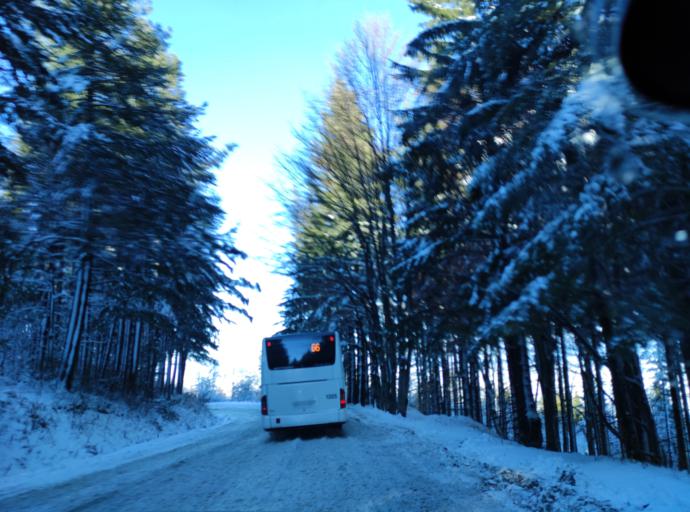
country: BG
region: Sofia-Capital
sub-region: Stolichna Obshtina
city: Sofia
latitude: 42.5937
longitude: 23.3123
